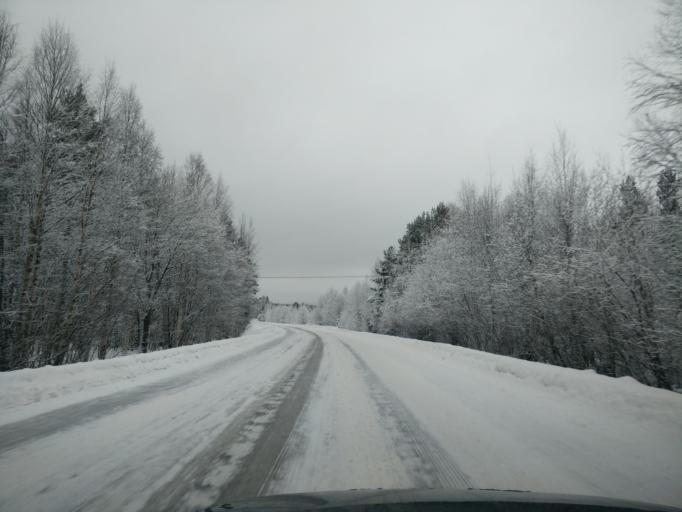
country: SE
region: Vaesternorrland
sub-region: Ange Kommun
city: Ange
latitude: 62.3968
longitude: 15.4393
